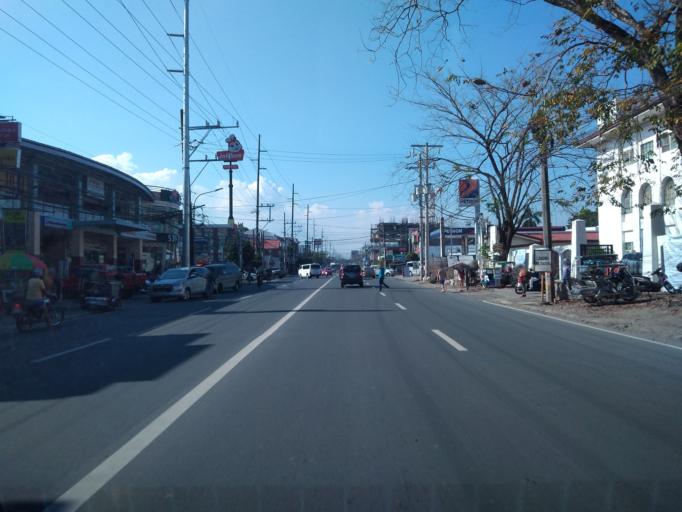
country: PH
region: Calabarzon
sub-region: Province of Laguna
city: Calamba
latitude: 14.1914
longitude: 121.1673
